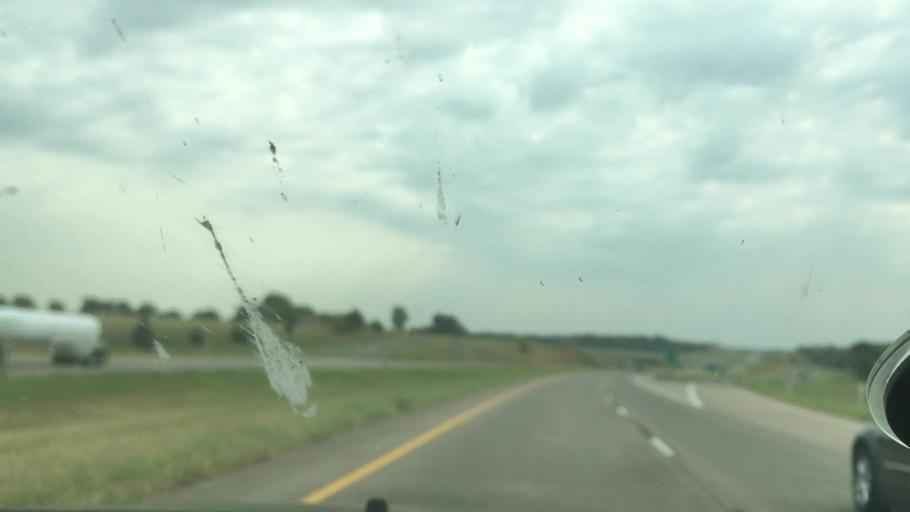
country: US
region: Texas
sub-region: Grayson County
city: Denison
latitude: 33.7873
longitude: -96.5766
